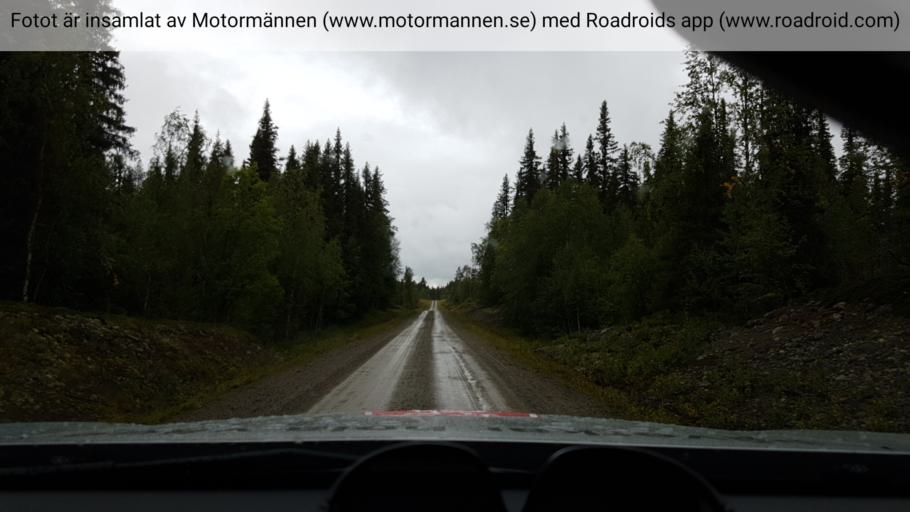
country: SE
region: Vaesterbotten
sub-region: Asele Kommun
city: Insjon
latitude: 64.7857
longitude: 17.5407
